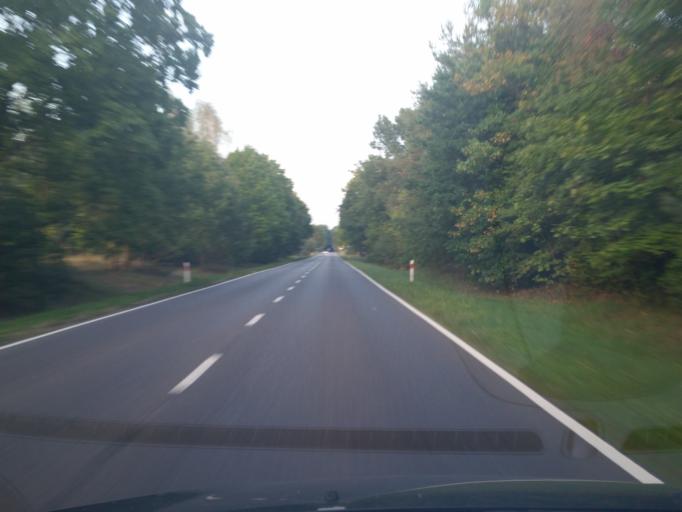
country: PL
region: Masovian Voivodeship
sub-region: Powiat nowodworski
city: Zakroczym
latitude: 52.3889
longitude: 20.6351
